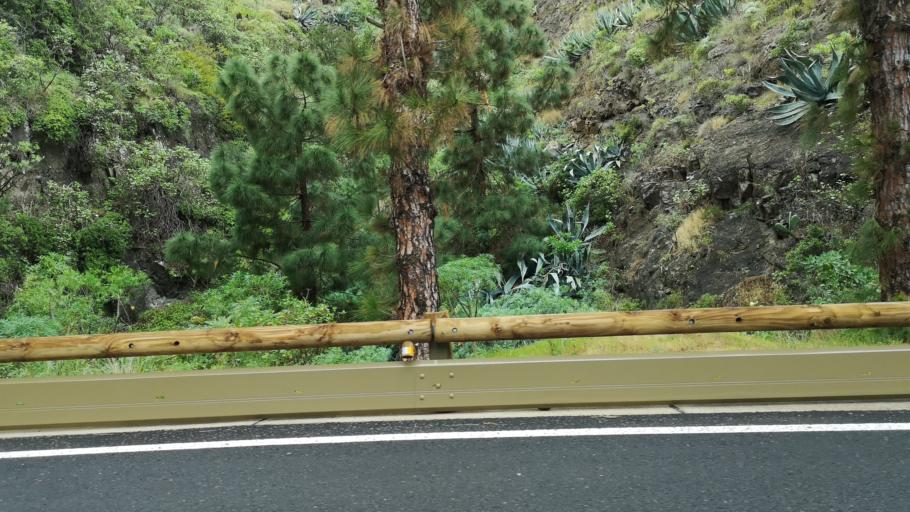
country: ES
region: Canary Islands
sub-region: Provincia de Santa Cruz de Tenerife
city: Hermigua
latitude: 28.1446
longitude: -17.2000
